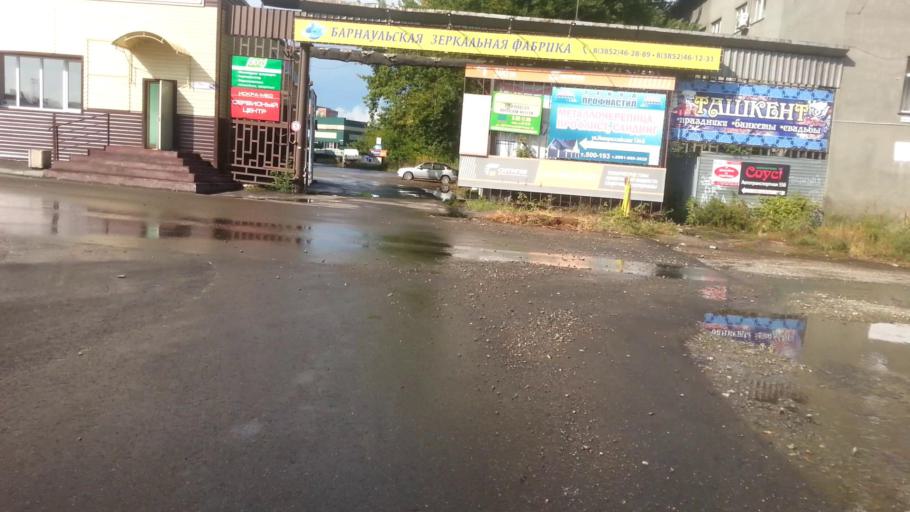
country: RU
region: Altai Krai
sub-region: Gorod Barnaulskiy
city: Barnaul
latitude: 53.3443
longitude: 83.7231
